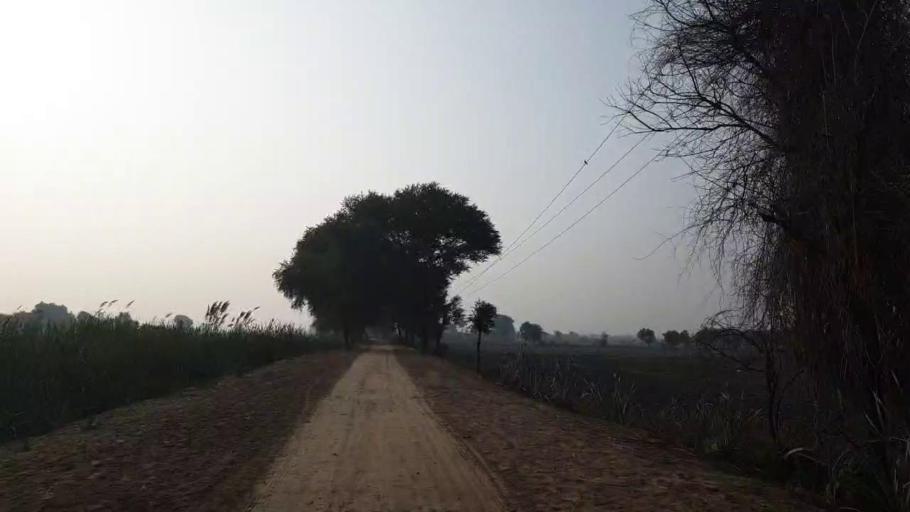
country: PK
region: Sindh
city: Tando Muhammad Khan
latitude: 25.1101
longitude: 68.5697
